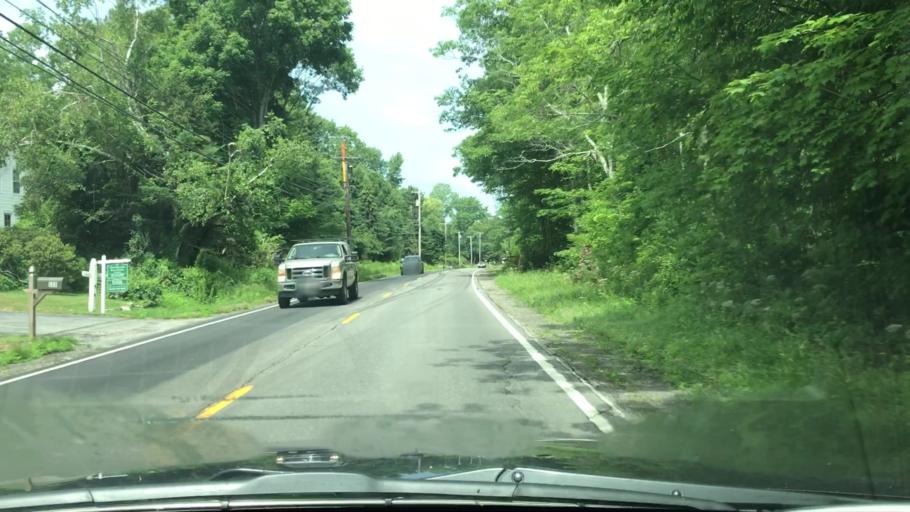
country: US
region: Maine
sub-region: Waldo County
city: Lincolnville
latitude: 44.2460
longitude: -69.0355
